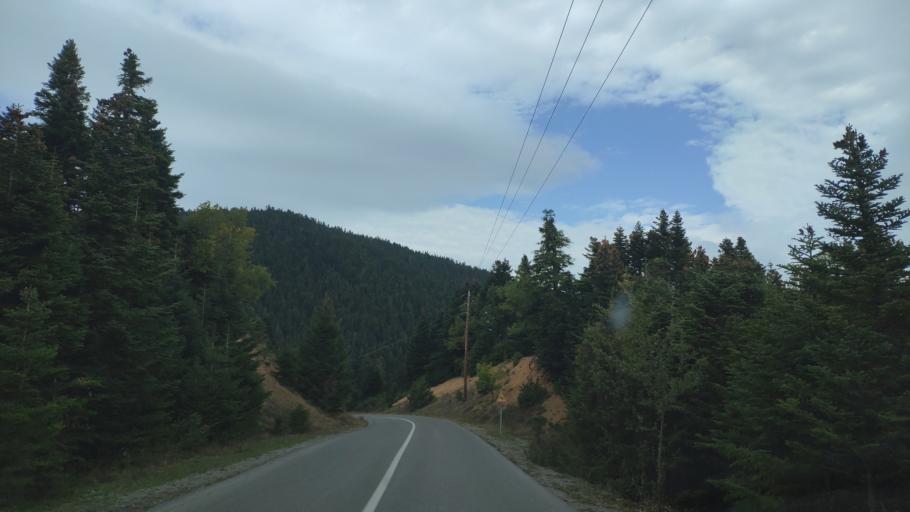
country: GR
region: Central Greece
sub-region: Nomos Fokidos
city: Amfissa
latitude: 38.7078
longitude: 22.3265
